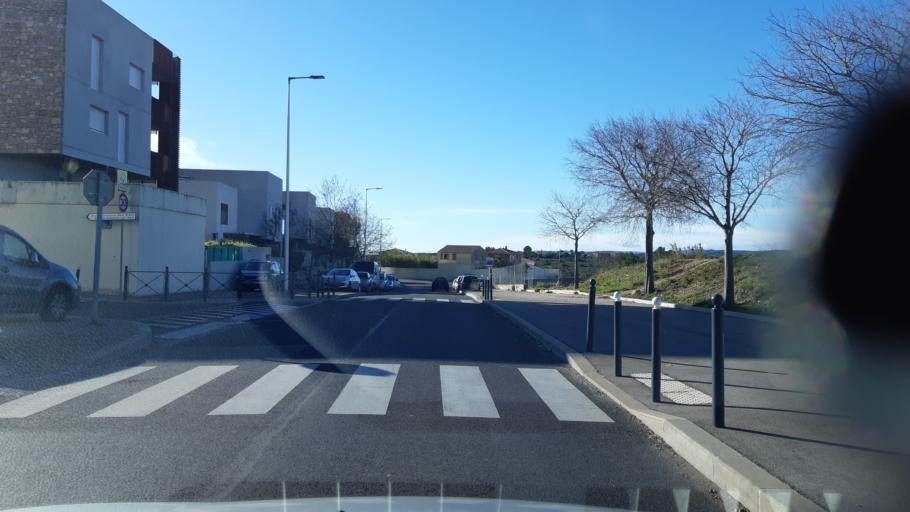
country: FR
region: Languedoc-Roussillon
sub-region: Departement de l'Herault
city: Grabels
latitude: 43.6410
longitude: 3.8117
